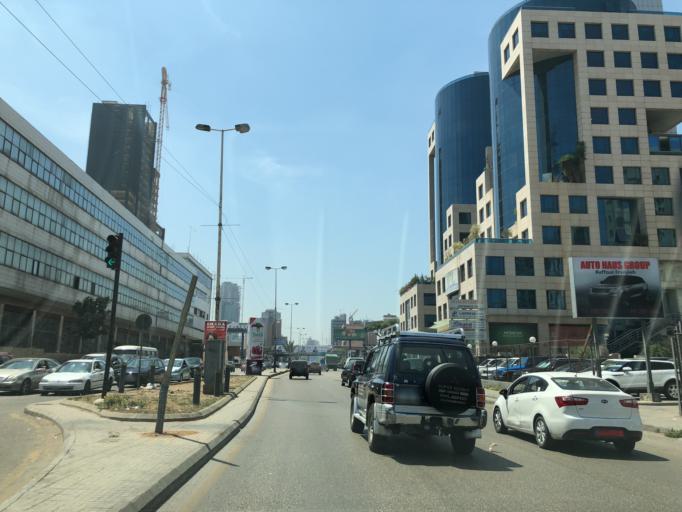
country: LB
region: Mont-Liban
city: Jdaidet el Matn
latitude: 33.8877
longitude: 35.5511
